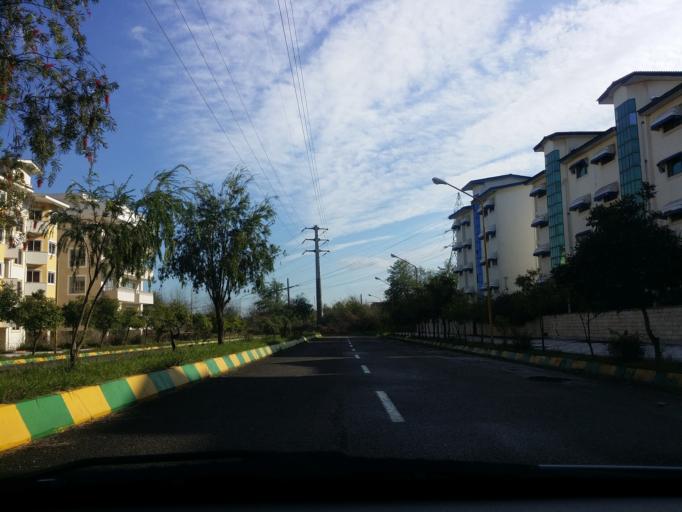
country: IR
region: Mazandaran
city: Chalus
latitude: 36.6742
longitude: 51.3127
